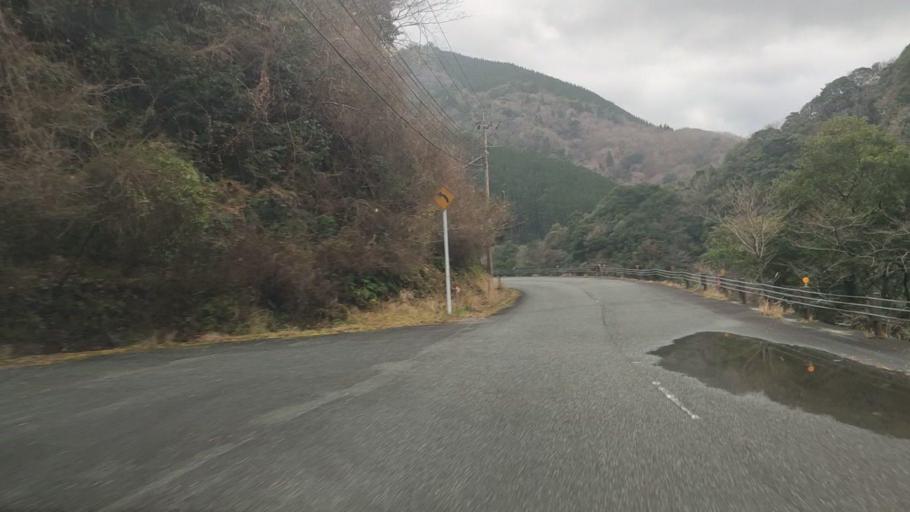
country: JP
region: Kumamoto
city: Matsubase
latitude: 32.5021
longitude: 130.9157
